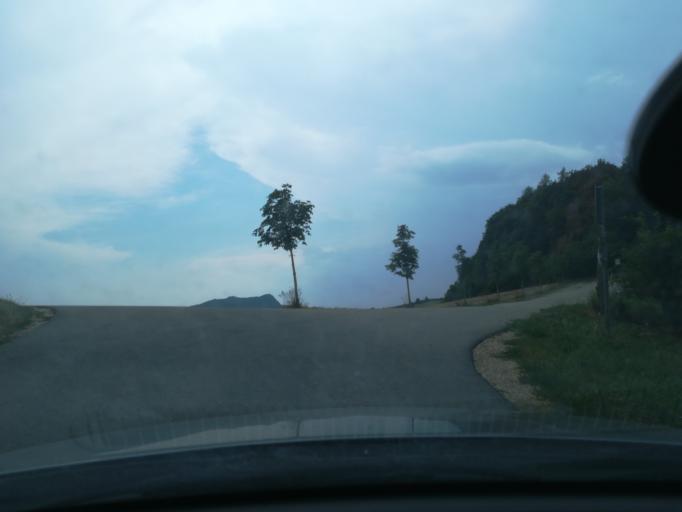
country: DE
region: Baden-Wuerttemberg
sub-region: Freiburg Region
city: Muhlhausen-Ehingen
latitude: 47.8040
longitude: 8.8017
